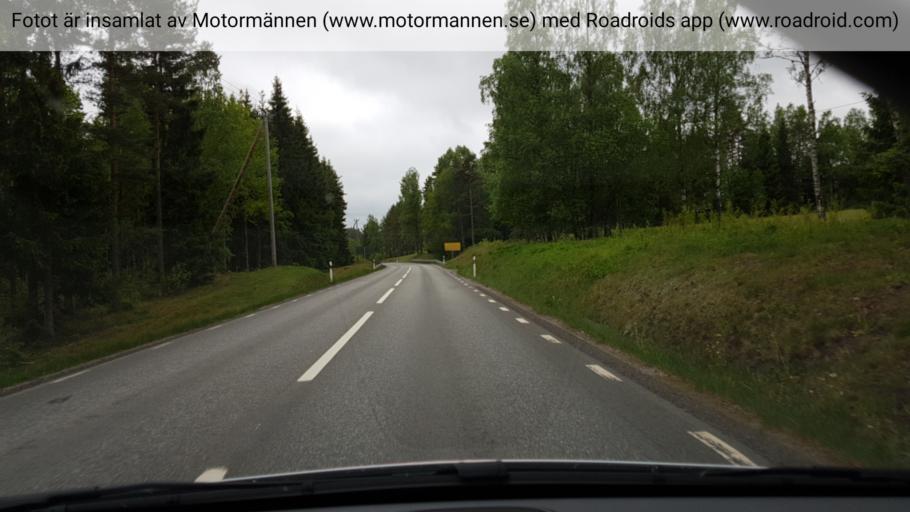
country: SE
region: Joenkoeping
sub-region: Mullsjo Kommun
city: Mullsjoe
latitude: 57.7923
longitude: 13.8384
